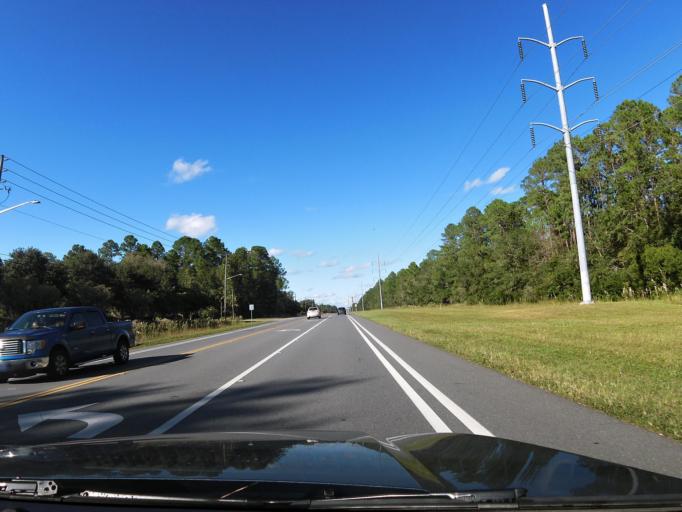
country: US
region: Florida
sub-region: Alachua County
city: Alachua
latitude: 29.7275
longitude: -82.3888
